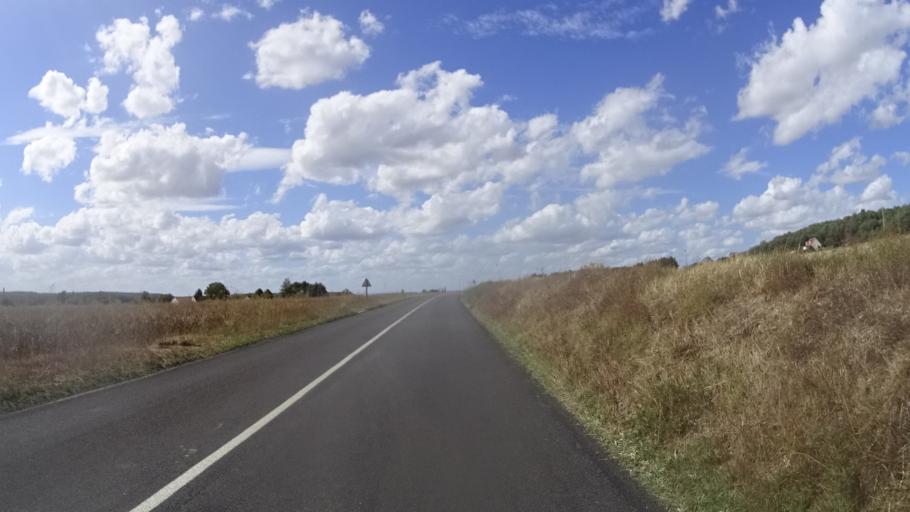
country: FR
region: Ile-de-France
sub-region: Departement de l'Essonne
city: La Ferte-Alais
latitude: 48.4565
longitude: 2.3576
